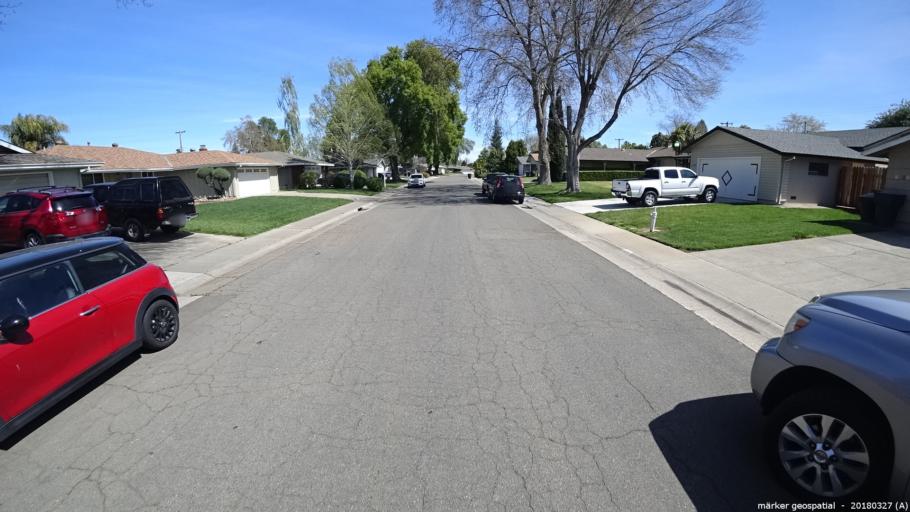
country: US
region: California
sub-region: Sacramento County
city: Rosemont
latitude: 38.5536
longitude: -121.3591
